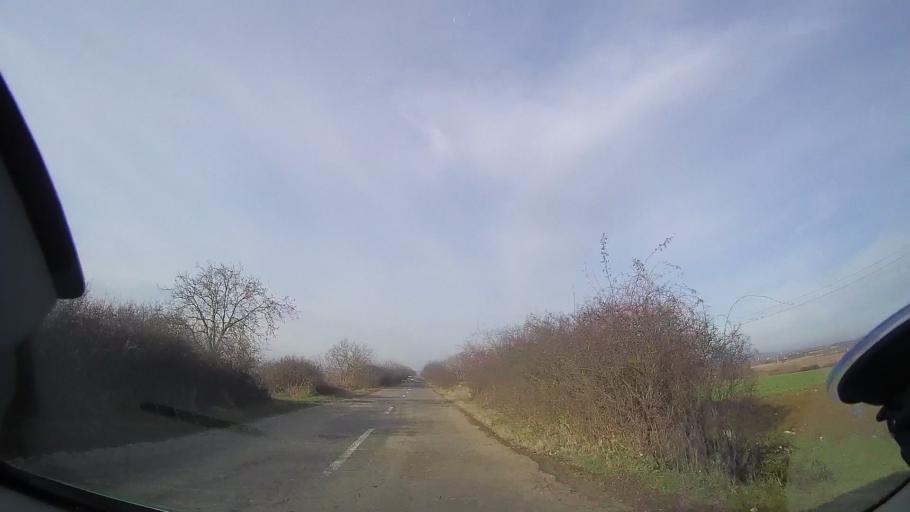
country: RO
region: Bihor
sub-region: Comuna Spinus
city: Spinus
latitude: 47.2138
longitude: 22.1770
